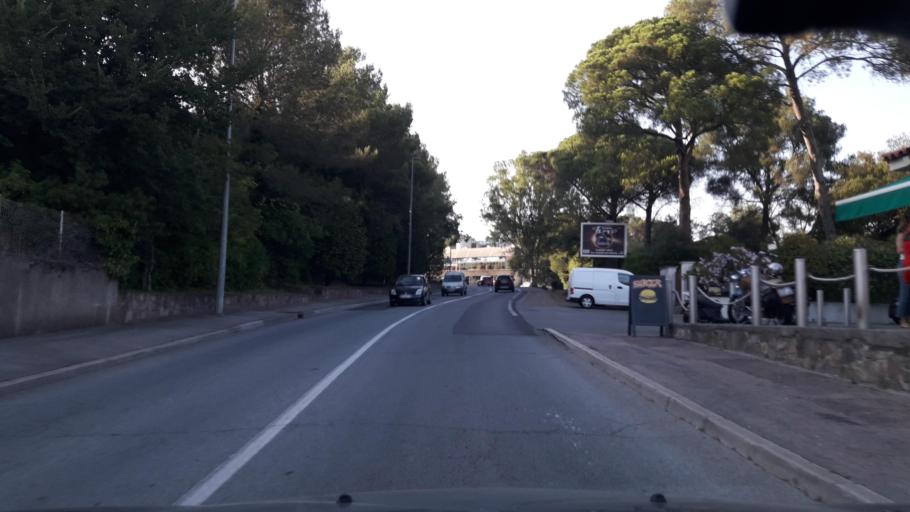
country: FR
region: Provence-Alpes-Cote d'Azur
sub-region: Departement du Var
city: Saint-Raphael
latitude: 43.4389
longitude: 6.7834
